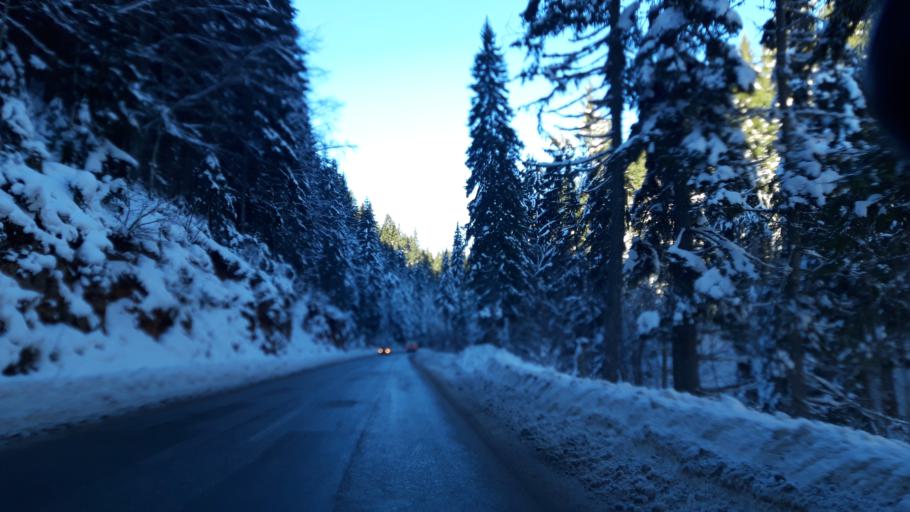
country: BA
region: Republika Srpska
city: Koran
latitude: 43.7487
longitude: 18.5548
